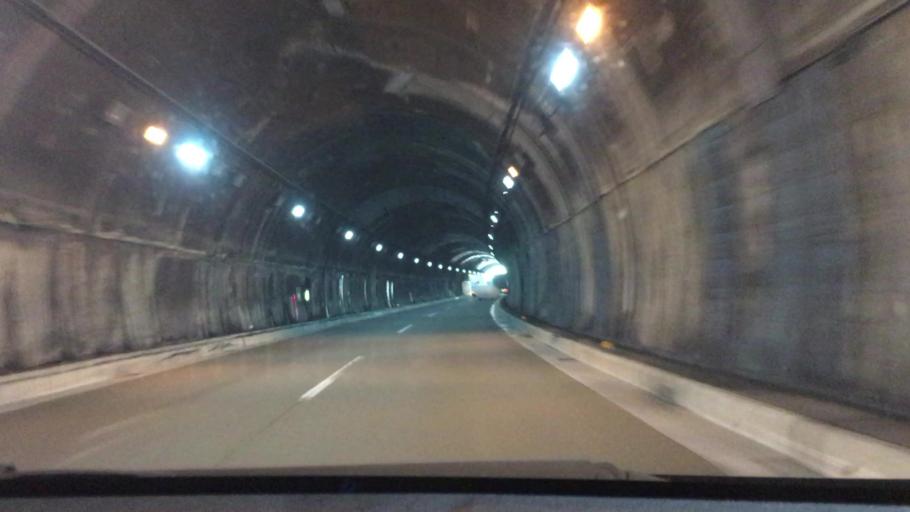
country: JP
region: Yamaguchi
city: Shimonoseki
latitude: 33.9536
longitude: 130.9806
